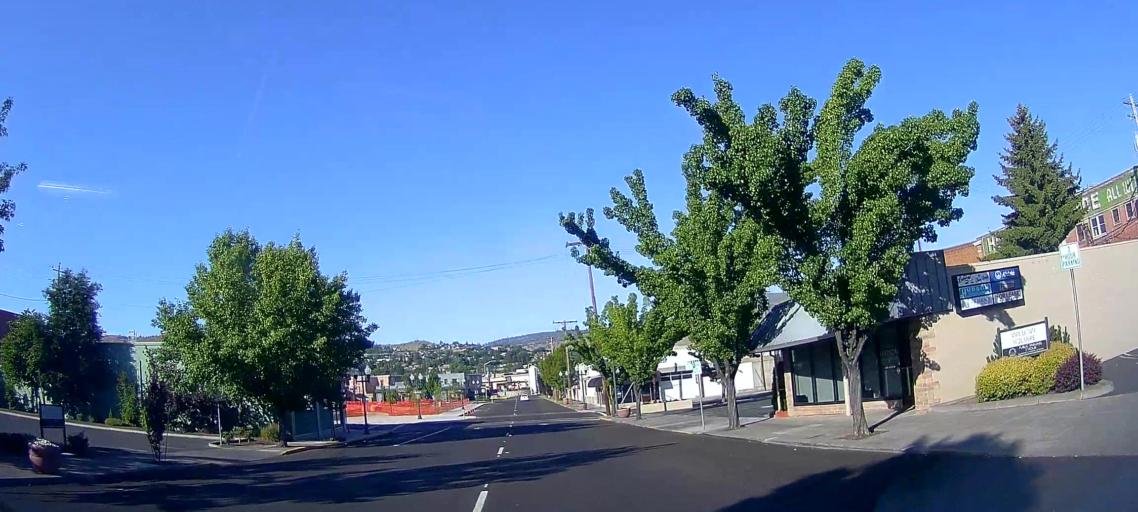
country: US
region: Oregon
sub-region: Klamath County
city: Klamath Falls
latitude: 42.2266
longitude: -121.7790
